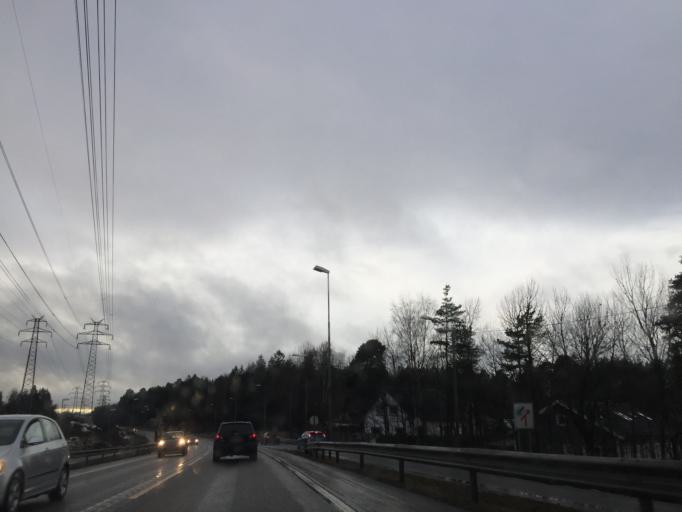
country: NO
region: Ostfold
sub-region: Moss
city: Moss
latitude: 59.4445
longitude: 10.6836
